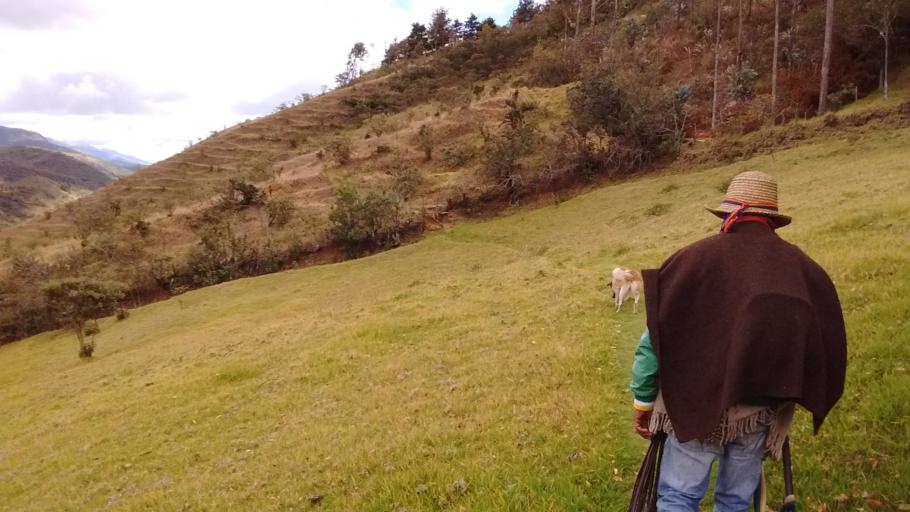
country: CO
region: Cauca
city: Silvia
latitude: 2.6206
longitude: -76.3778
